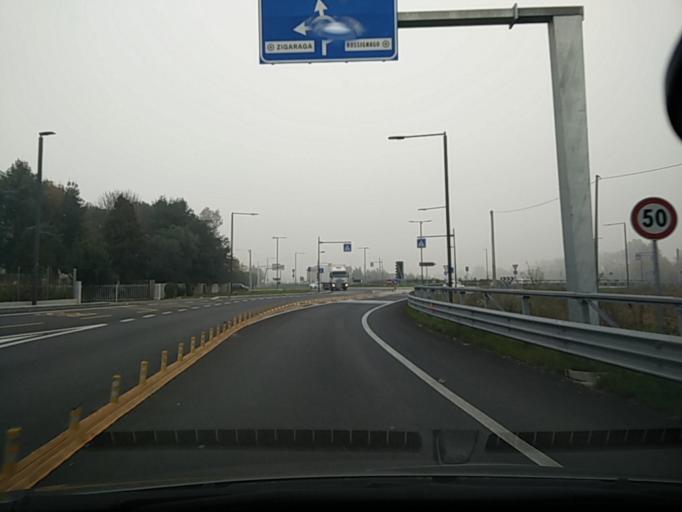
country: IT
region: Veneto
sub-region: Provincia di Venezia
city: Maerne
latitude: 45.5066
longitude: 12.1473
